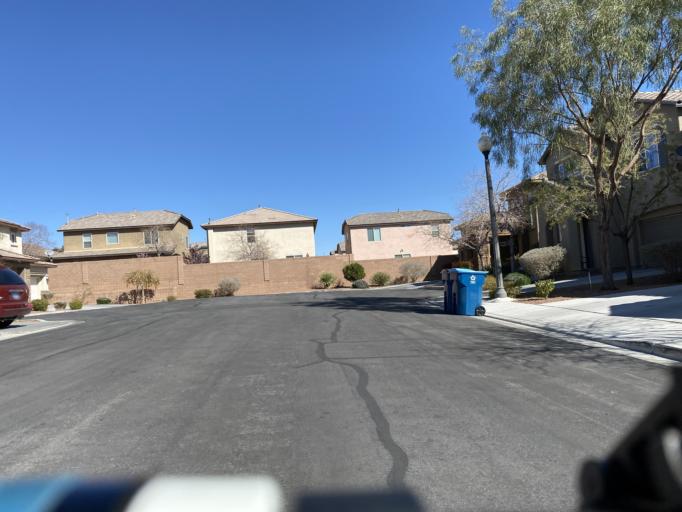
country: US
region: Nevada
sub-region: Clark County
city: Summerlin South
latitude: 36.2902
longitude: -115.3218
